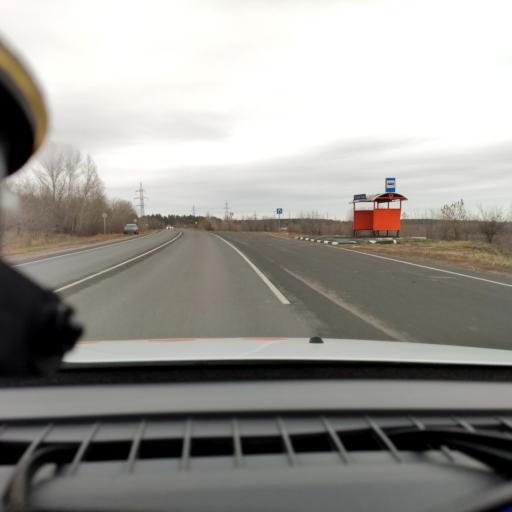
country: RU
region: Samara
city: Samara
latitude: 53.1234
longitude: 50.1953
